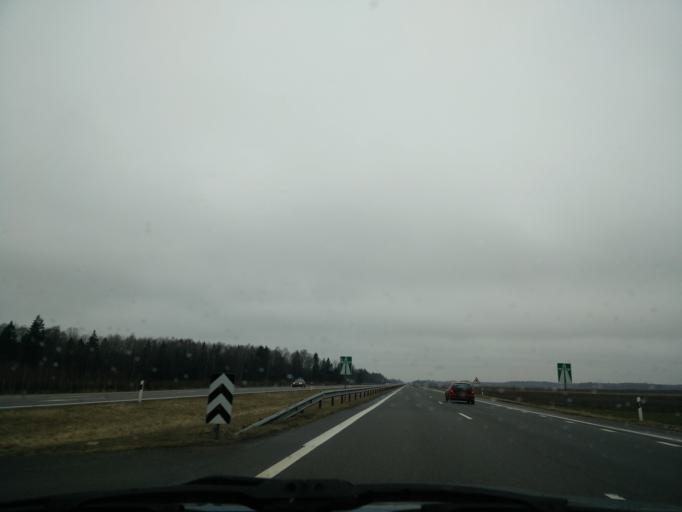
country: LT
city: Raseiniai
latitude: 55.3743
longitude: 22.9484
